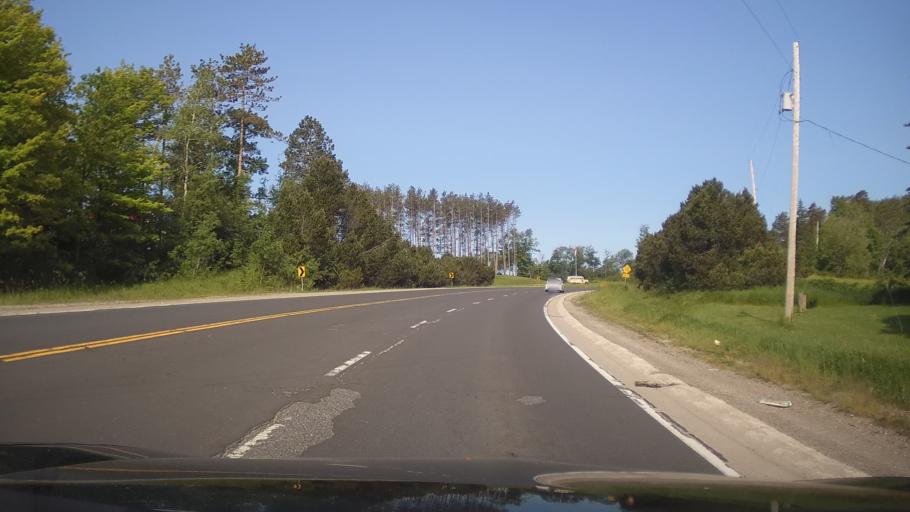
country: CA
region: Ontario
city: Omemee
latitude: 44.2925
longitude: -78.5886
